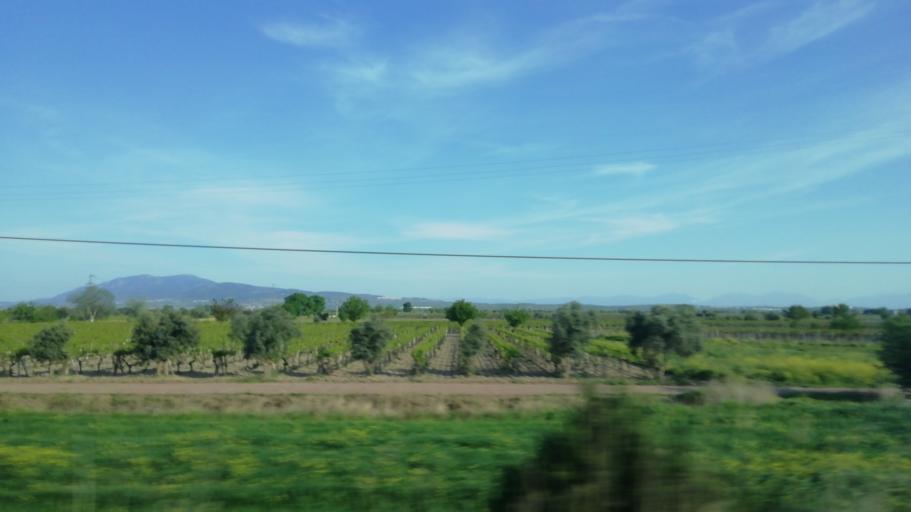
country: TR
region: Manisa
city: Saruhanli
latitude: 38.7337
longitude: 27.5886
